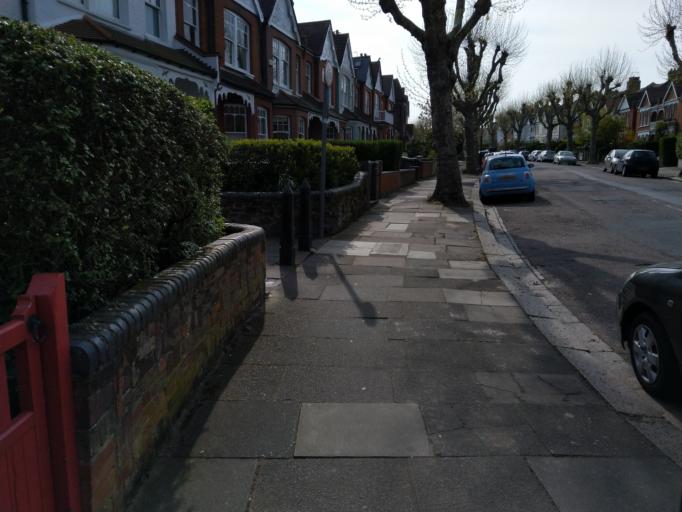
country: GB
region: England
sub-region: Greater London
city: Crouch End
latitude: 51.5858
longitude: -0.1279
